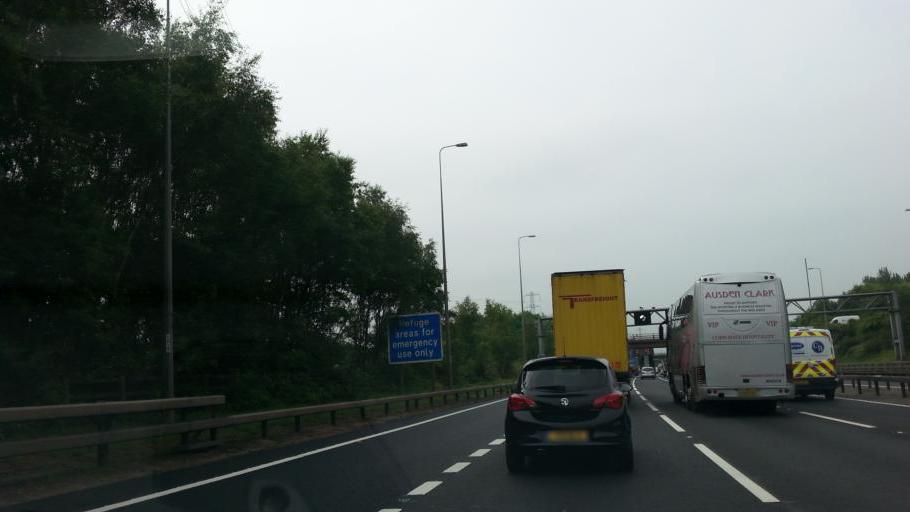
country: GB
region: England
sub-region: Solihull
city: Chelmsley Wood
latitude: 52.4678
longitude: -1.7102
